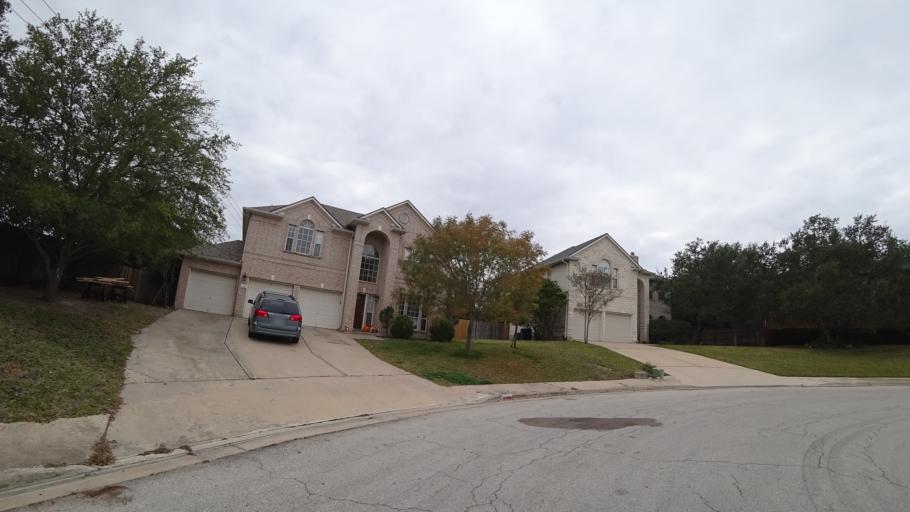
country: US
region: Texas
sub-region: Travis County
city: Bee Cave
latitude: 30.3119
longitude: -97.9139
